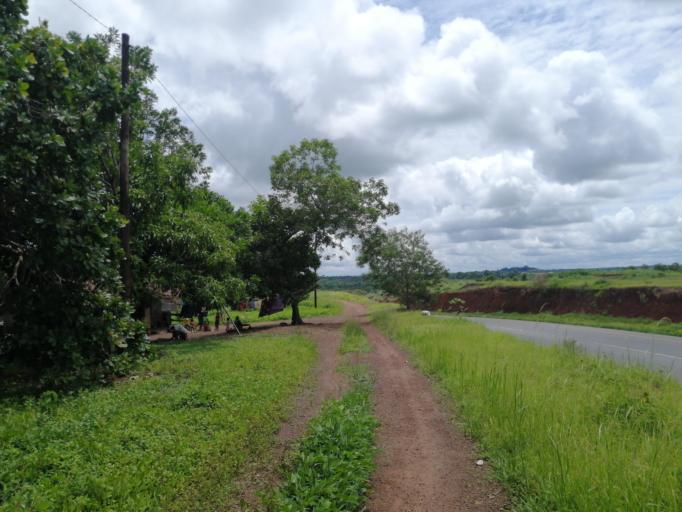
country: SL
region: Northern Province
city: Port Loko
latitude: 8.7801
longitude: -12.7976
